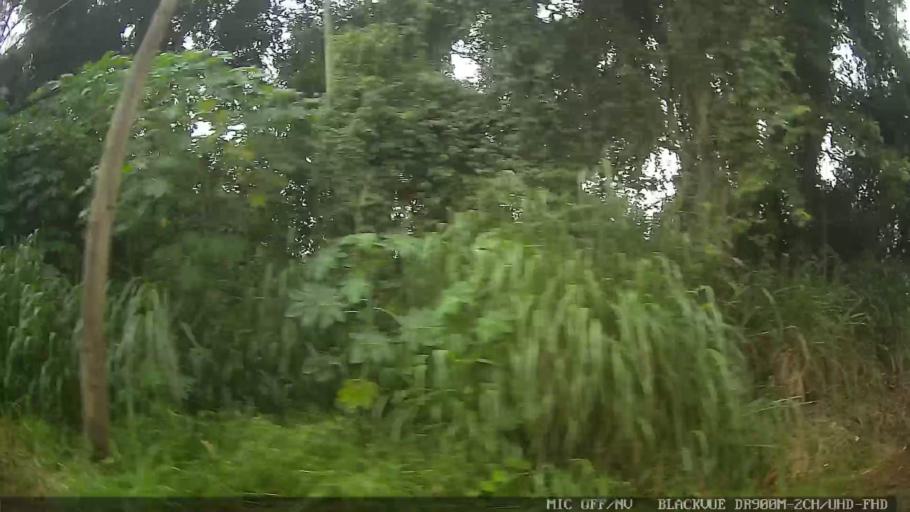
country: BR
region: Sao Paulo
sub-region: Atibaia
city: Atibaia
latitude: -23.1643
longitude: -46.6234
